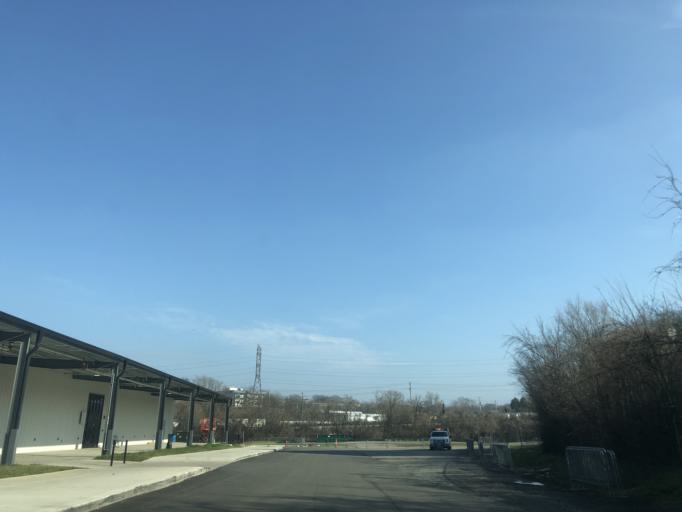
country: US
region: Tennessee
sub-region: Davidson County
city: Nashville
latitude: 36.1326
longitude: -86.7617
